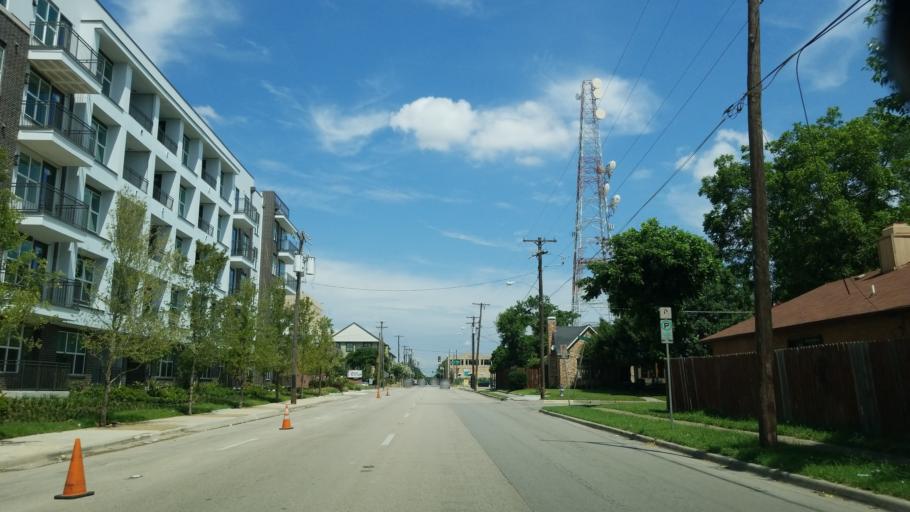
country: US
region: Texas
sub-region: Dallas County
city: Dallas
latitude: 32.7969
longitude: -96.7770
